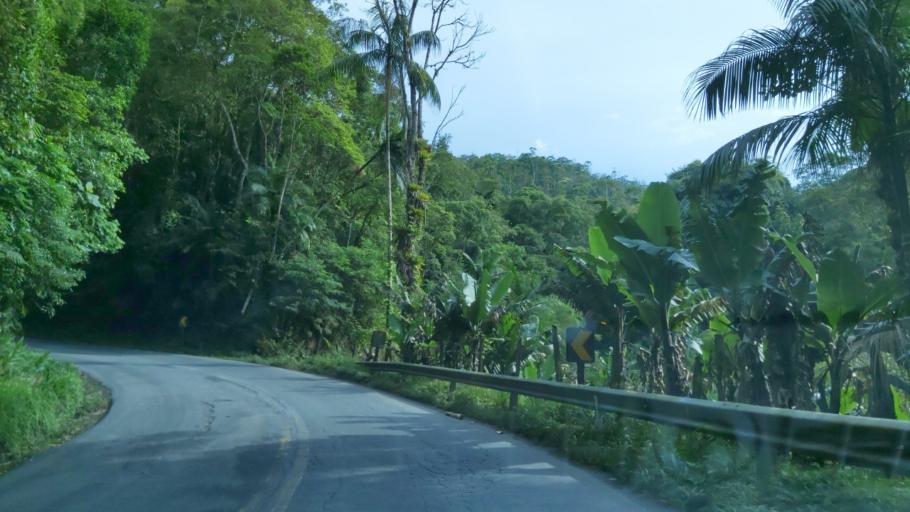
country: BR
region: Sao Paulo
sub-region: Miracatu
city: Miracatu
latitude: -24.0542
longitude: -47.5708
